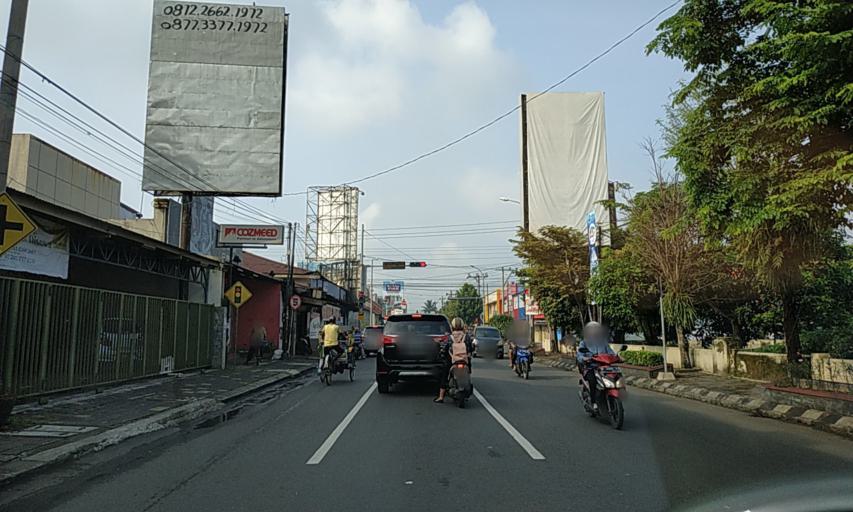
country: ID
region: Central Java
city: Purwokerto
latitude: -7.4227
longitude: 109.2440
